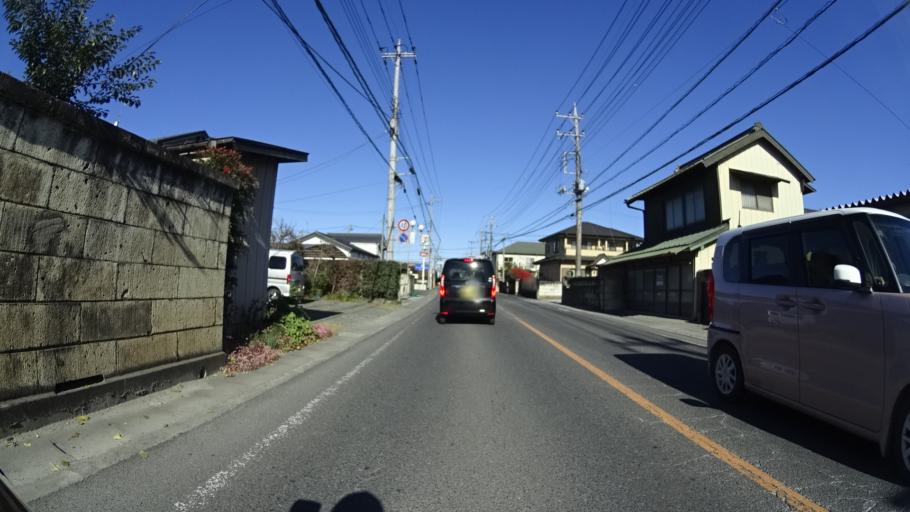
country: JP
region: Tochigi
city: Tochigi
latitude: 36.4060
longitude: 139.7432
